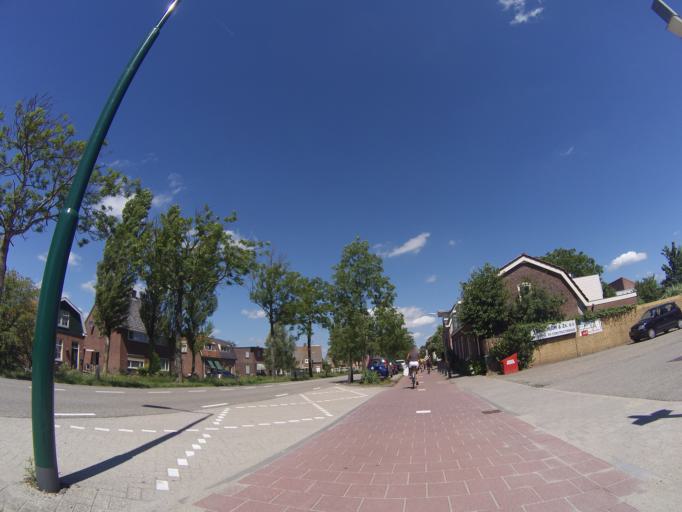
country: NL
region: Utrecht
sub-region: Gemeente Utrecht
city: Utrecht
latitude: 52.1224
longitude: 5.1427
